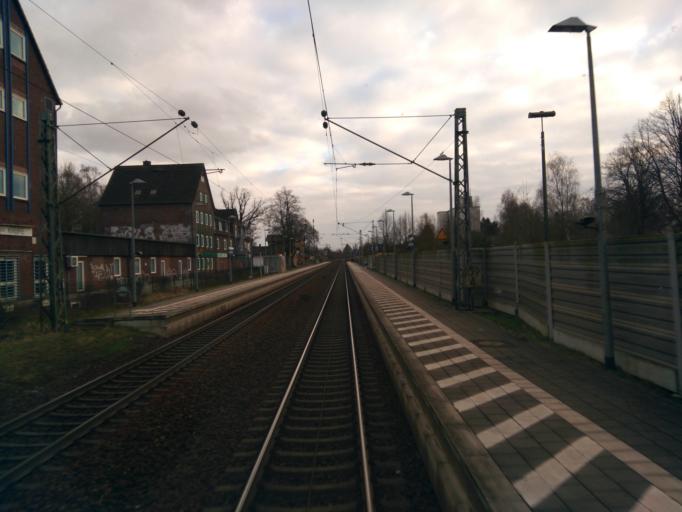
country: DE
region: Lower Saxony
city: Bad Bevensen
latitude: 53.0797
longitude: 10.5728
